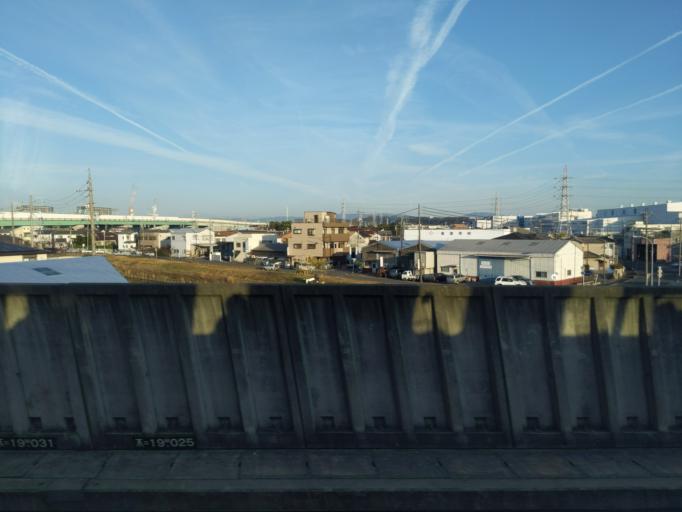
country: JP
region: Aichi
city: Kasugai
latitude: 35.2230
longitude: 136.9517
